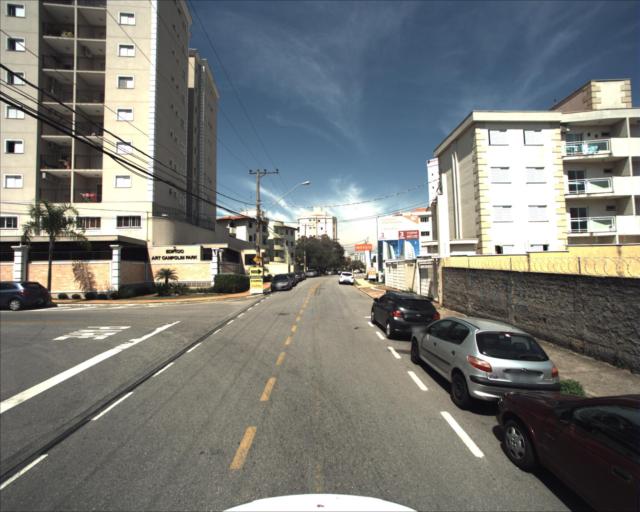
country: BR
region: Sao Paulo
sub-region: Votorantim
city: Votorantim
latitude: -23.5331
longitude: -47.4673
